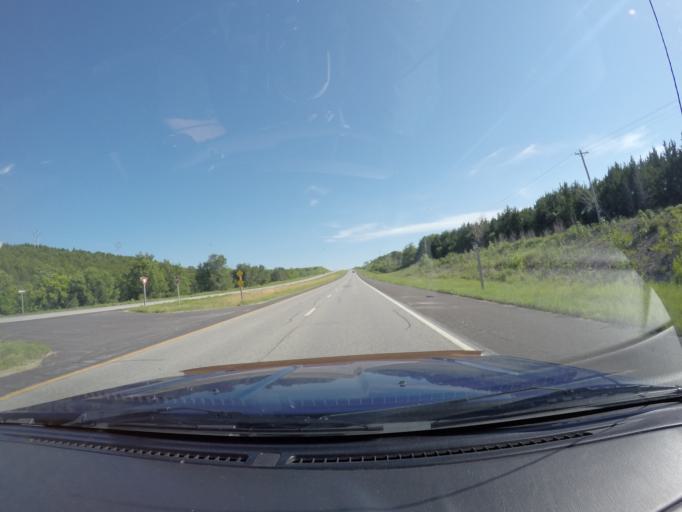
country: US
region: Kansas
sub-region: Riley County
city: Manhattan
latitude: 39.1486
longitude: -96.5386
